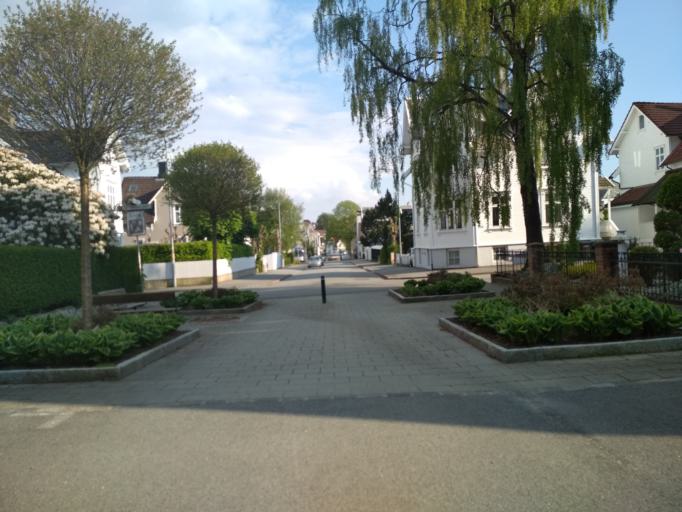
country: NO
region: Rogaland
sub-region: Stavanger
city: Stavanger
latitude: 58.9652
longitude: 5.7246
